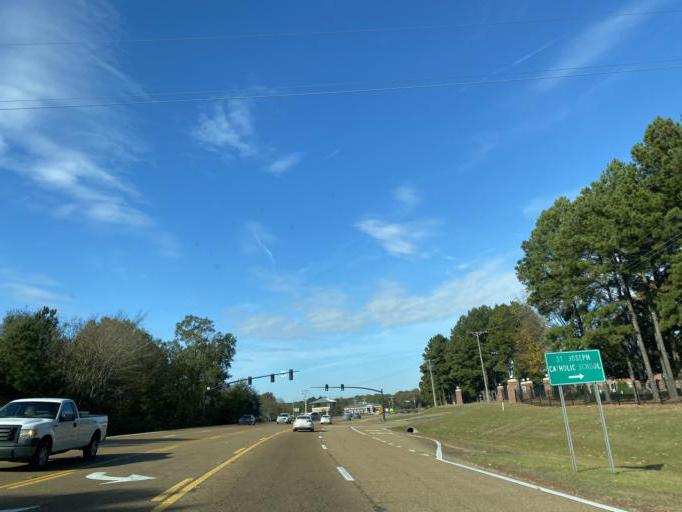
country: US
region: Mississippi
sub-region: Madison County
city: Madison
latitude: 32.4728
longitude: -90.1467
